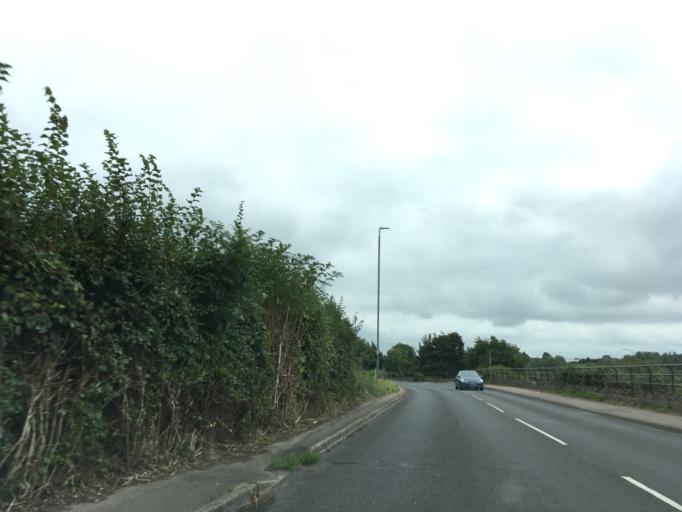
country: GB
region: England
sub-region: Bath and North East Somerset
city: Keynsham
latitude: 51.4230
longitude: -2.4876
